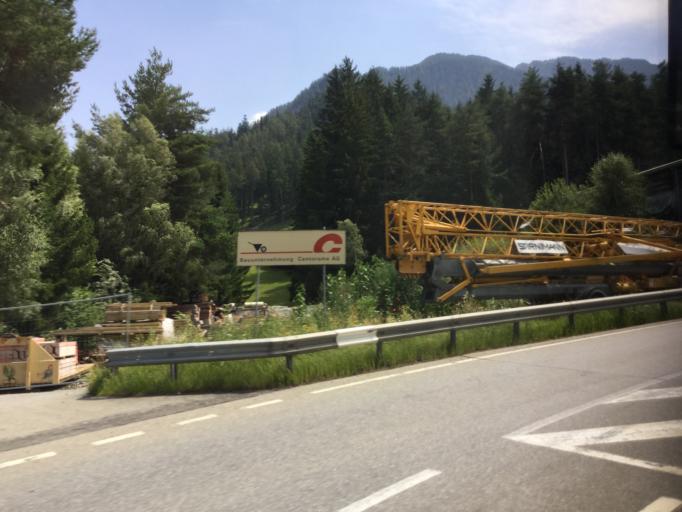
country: CH
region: Grisons
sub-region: Albula District
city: Tiefencastel
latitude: 46.6538
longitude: 9.5762
